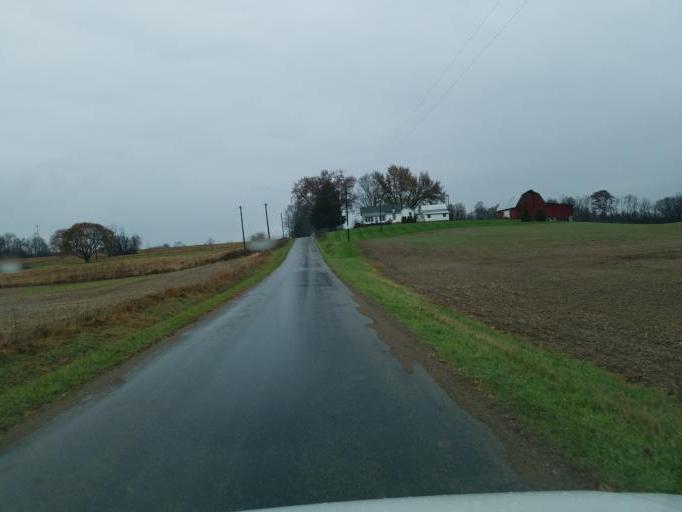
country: US
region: Ohio
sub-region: Knox County
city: Fredericktown
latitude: 40.4777
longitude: -82.5768
